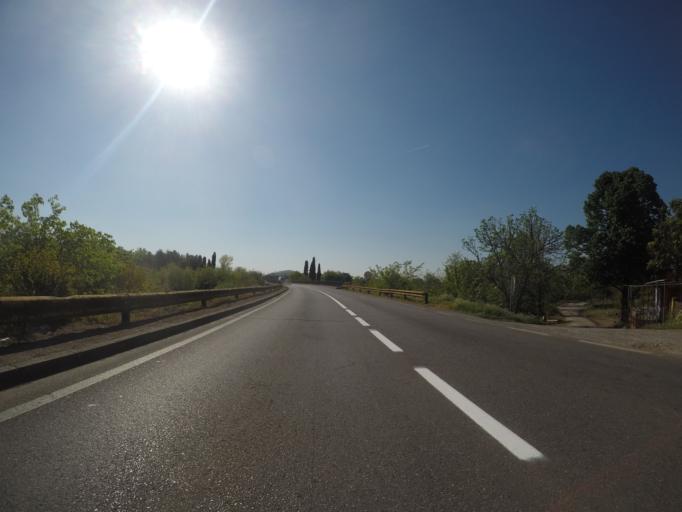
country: ME
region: Podgorica
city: Podgorica
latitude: 42.4448
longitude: 19.2033
